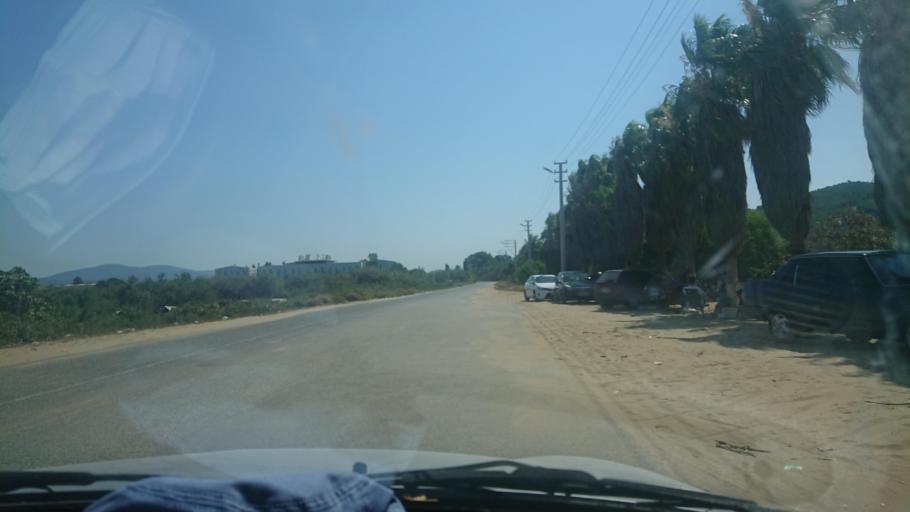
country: TR
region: Aydin
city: Kusadasi
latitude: 37.9437
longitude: 27.2748
